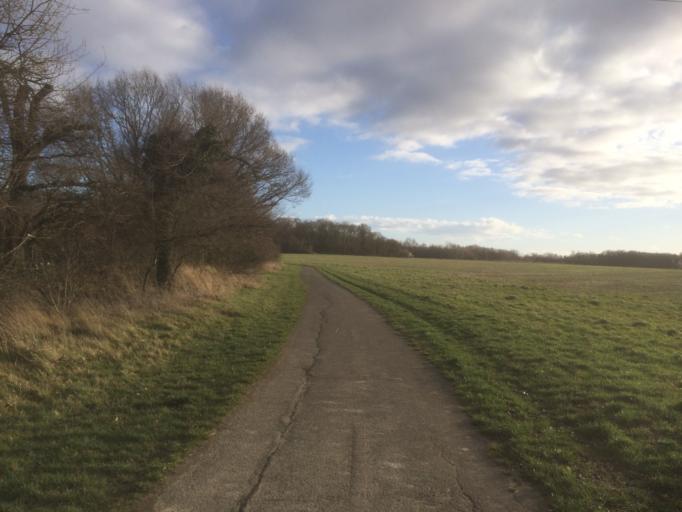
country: FR
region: Ile-de-France
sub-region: Departement de l'Essonne
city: Vauhallan
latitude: 48.7439
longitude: 2.2092
